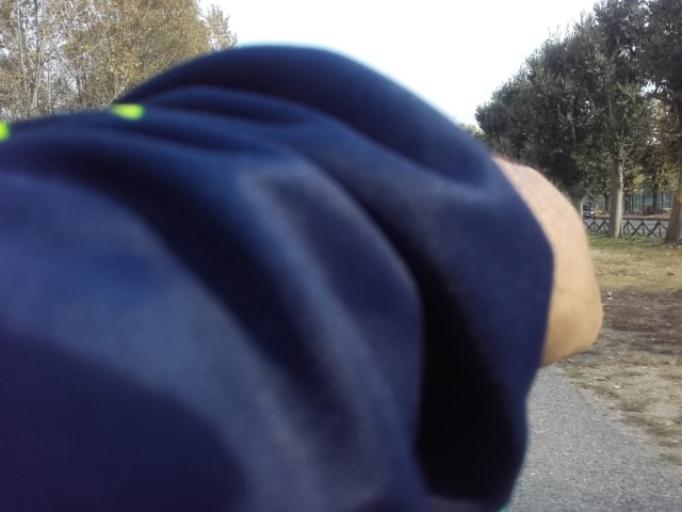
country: IT
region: Piedmont
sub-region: Provincia di Torino
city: San Mauro Torinese
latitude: 45.0949
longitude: 7.7511
